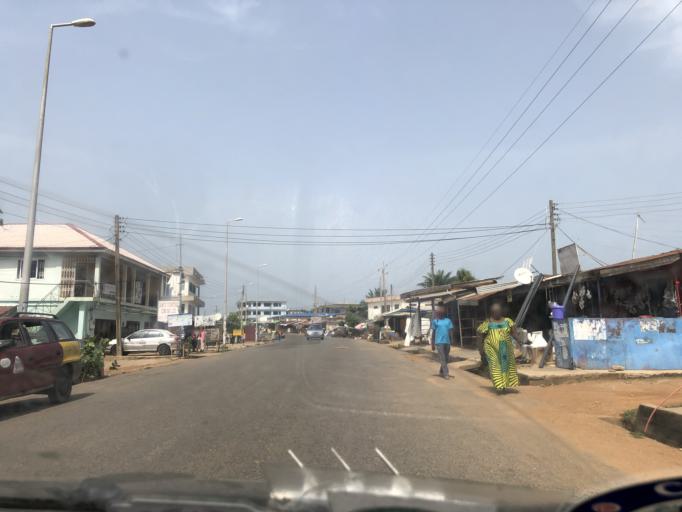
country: GH
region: Eastern
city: Koforidua
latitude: 6.0977
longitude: -0.2644
